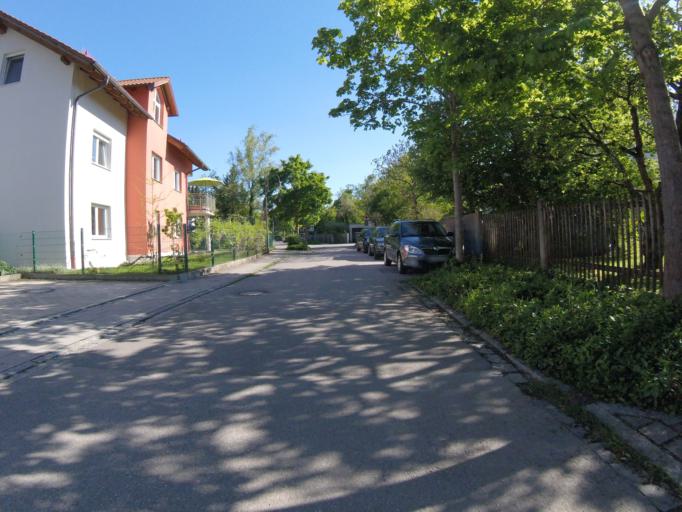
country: DE
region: Bavaria
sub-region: Upper Bavaria
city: Ottobrunn
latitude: 48.0710
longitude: 11.6613
